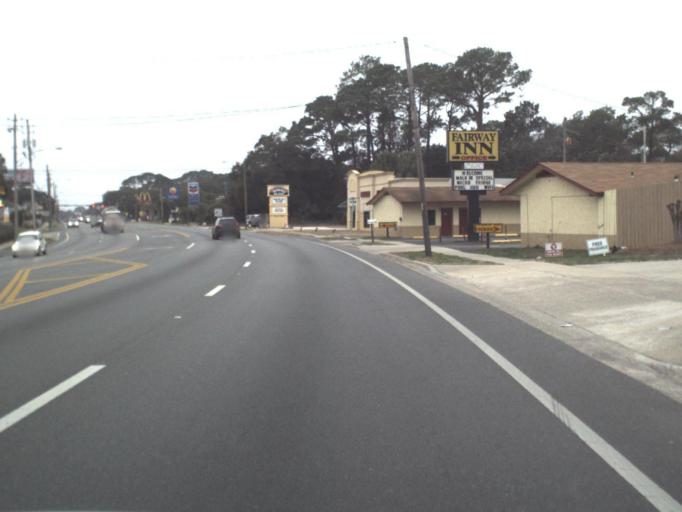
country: US
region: Florida
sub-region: Bay County
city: Pretty Bayou
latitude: 30.1806
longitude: -85.7047
